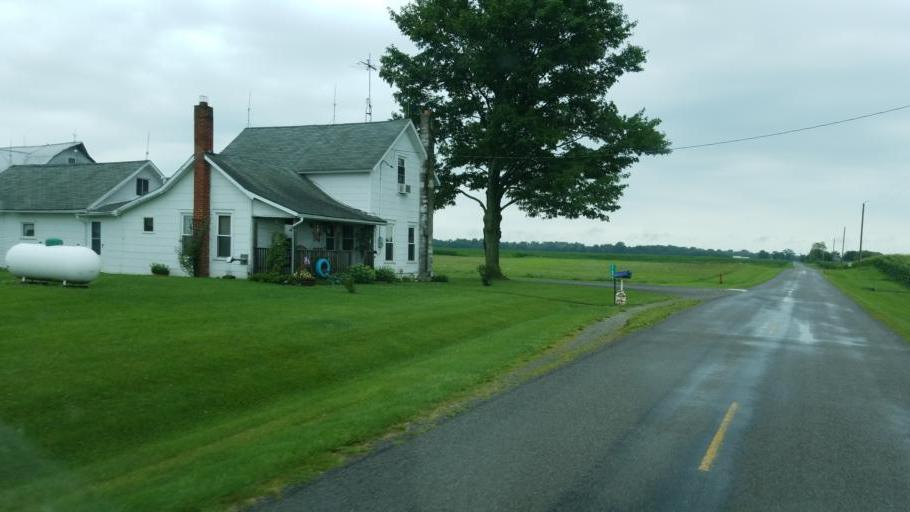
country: US
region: Ohio
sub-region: Union County
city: Richwood
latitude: 40.5124
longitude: -83.4606
